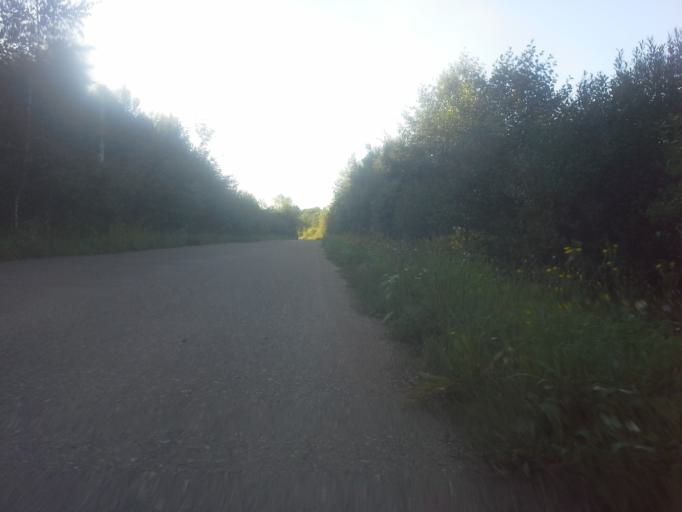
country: RU
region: Moskovskaya
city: Kievskij
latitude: 55.3879
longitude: 36.9033
